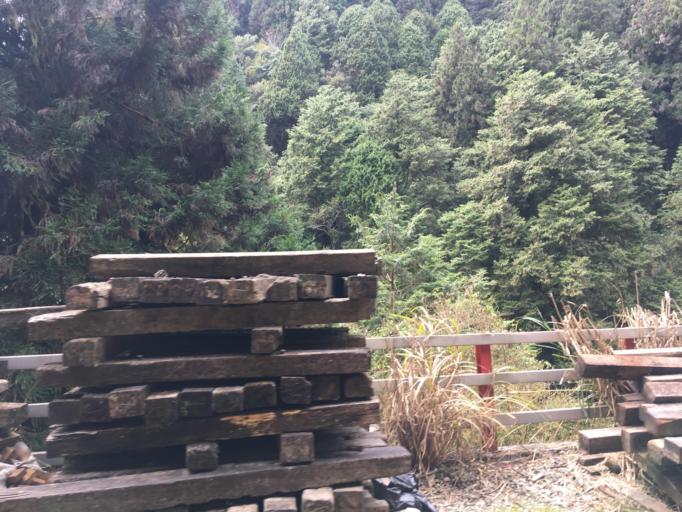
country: TW
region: Taiwan
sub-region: Yilan
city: Yilan
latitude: 24.4935
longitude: 121.5337
